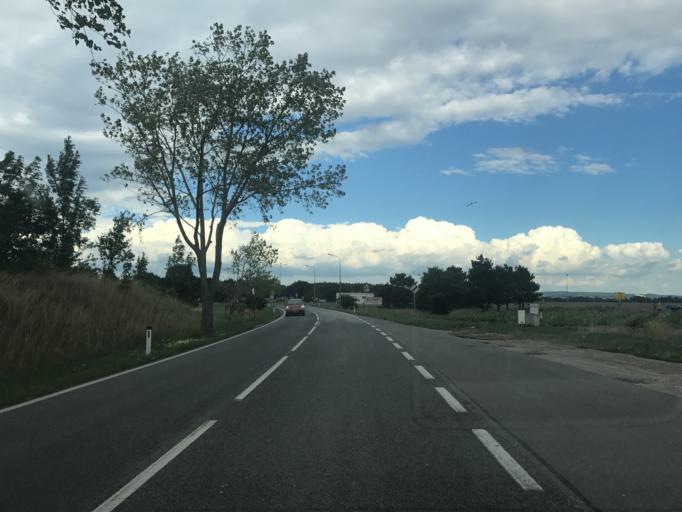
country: AT
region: Lower Austria
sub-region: Politischer Bezirk Wiener Neustadt
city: Felixdorf
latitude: 47.8713
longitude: 16.2228
